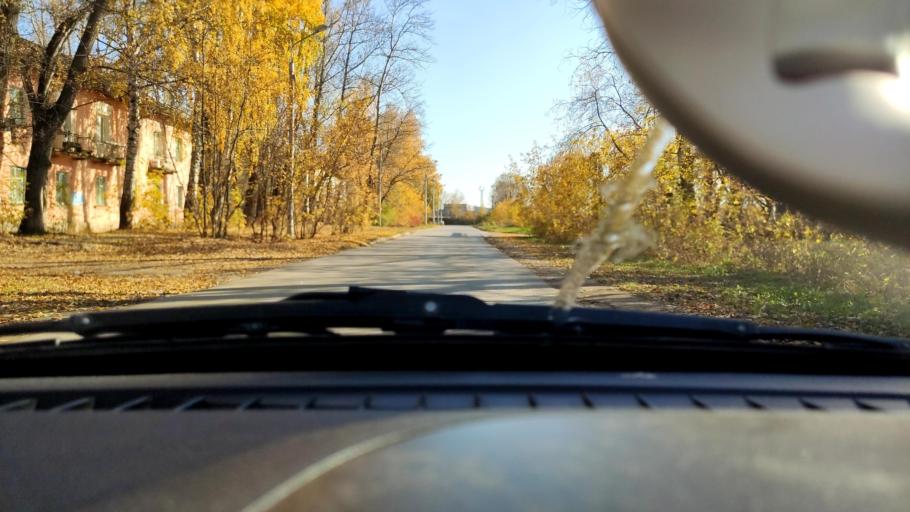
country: RU
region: Perm
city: Kondratovo
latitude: 58.0395
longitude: 56.1033
